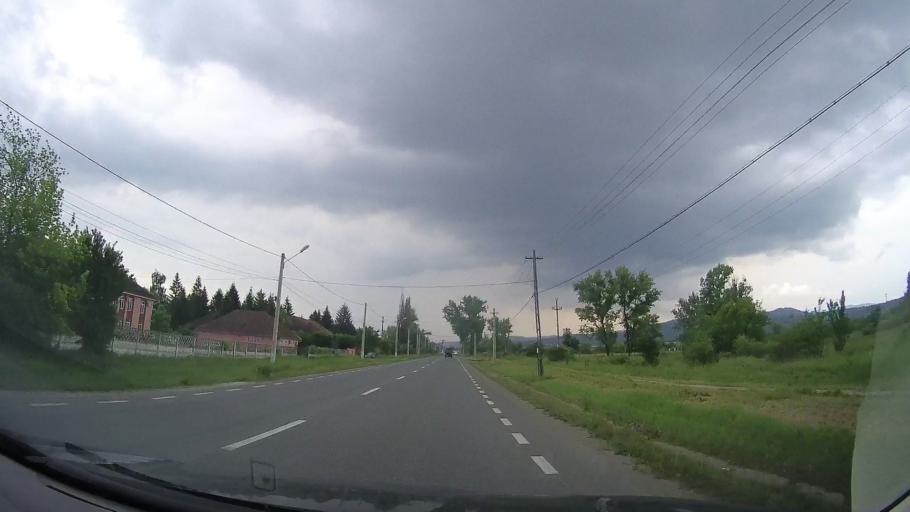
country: RO
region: Caras-Severin
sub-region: Municipiul Caransebes
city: Caransebes
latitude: 45.4337
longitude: 22.1945
